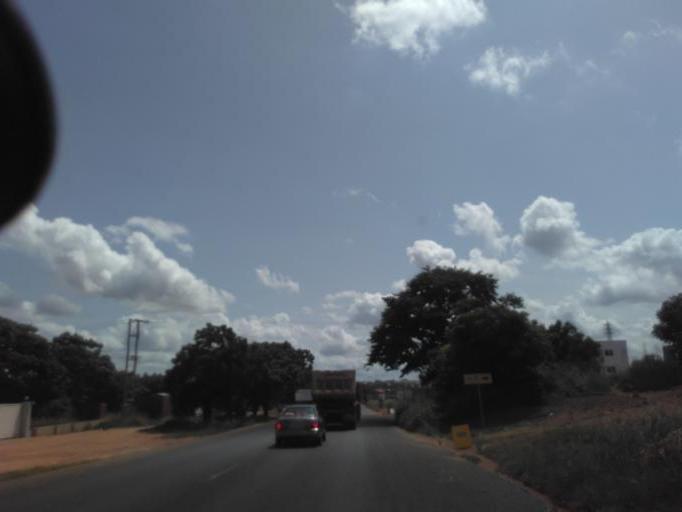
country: GH
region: Eastern
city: Aburi
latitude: 5.7830
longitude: -0.1335
